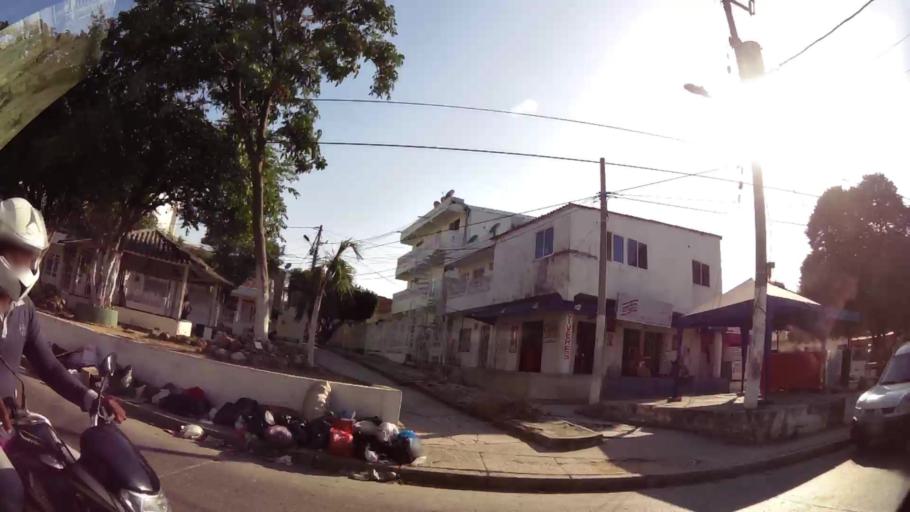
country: CO
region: Bolivar
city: Cartagena
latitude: 10.3835
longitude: -75.4840
